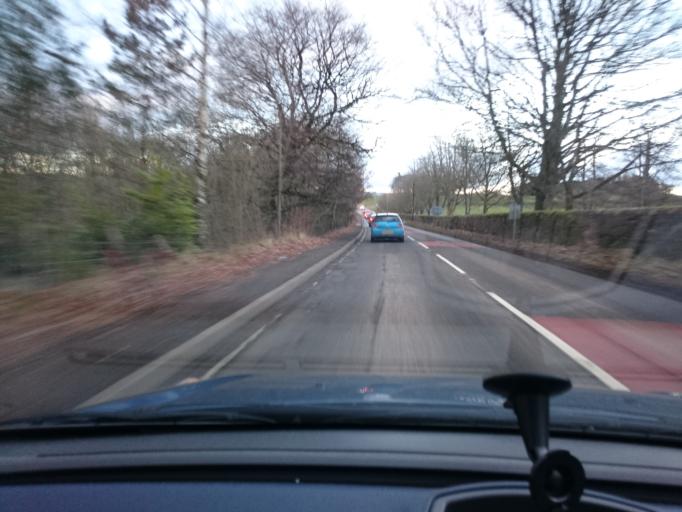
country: GB
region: Scotland
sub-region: Stirling
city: Doune
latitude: 56.1873
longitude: -4.0441
